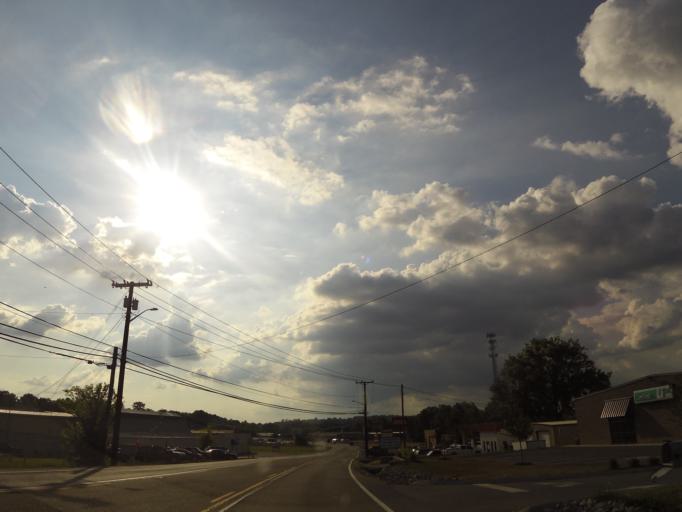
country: US
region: Tennessee
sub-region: Montgomery County
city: Clarksville
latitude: 36.5394
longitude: -87.3400
